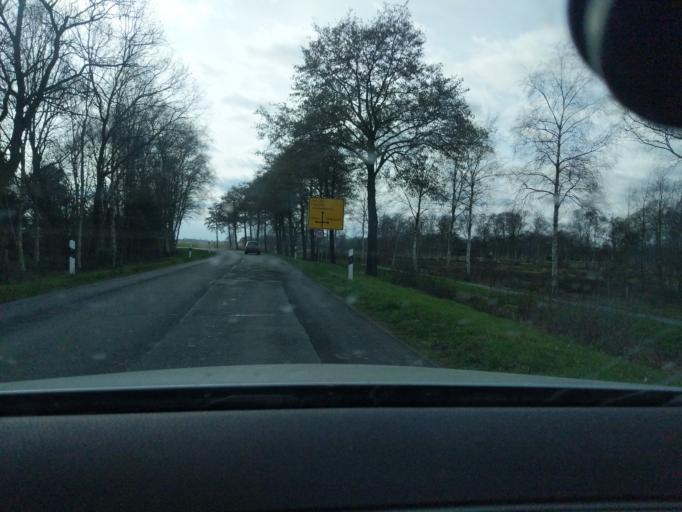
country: DE
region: Lower Saxony
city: Drochtersen
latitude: 53.6698
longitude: 9.3854
